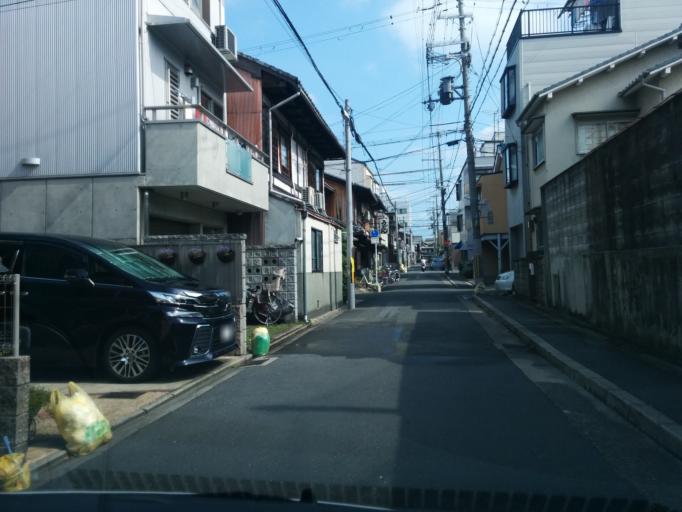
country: JP
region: Kyoto
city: Muko
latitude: 34.9876
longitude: 135.7346
